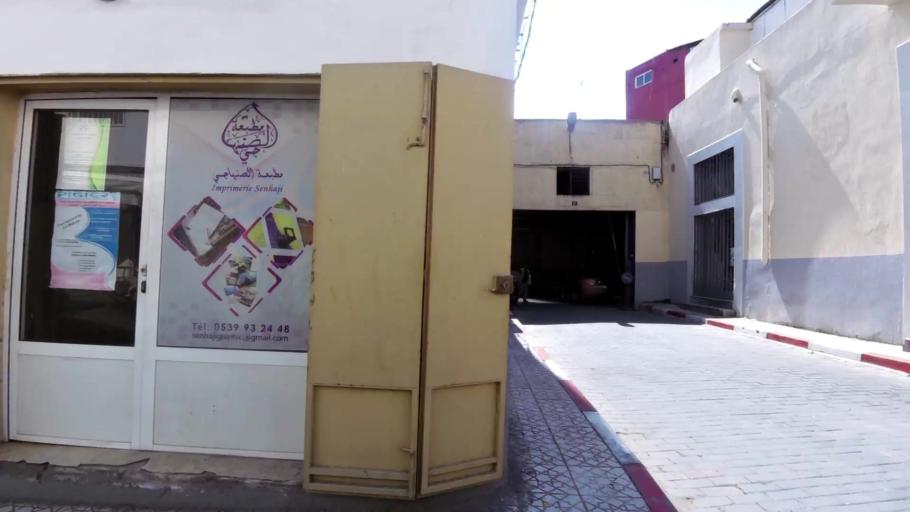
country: MA
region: Tanger-Tetouan
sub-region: Tanger-Assilah
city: Tangier
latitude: 35.7868
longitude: -5.8142
